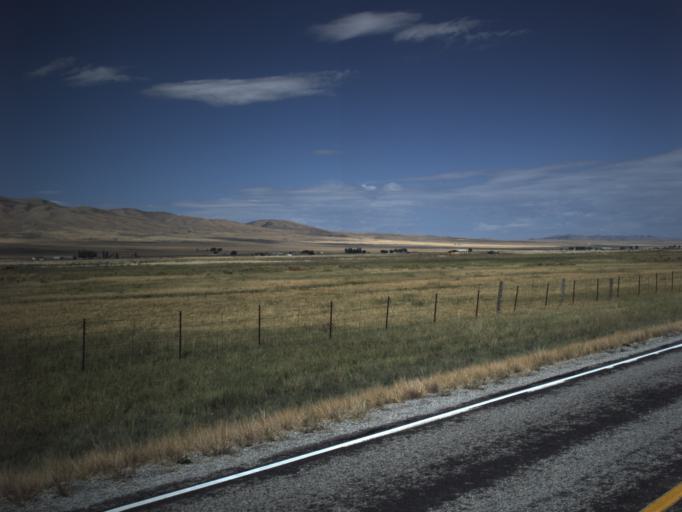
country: US
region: Utah
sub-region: Box Elder County
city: Tremonton
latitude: 41.7552
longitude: -112.4347
